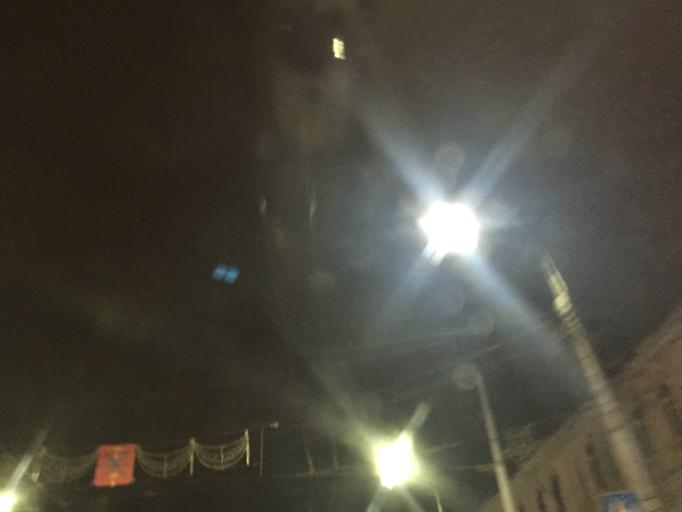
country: RU
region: Tula
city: Tula
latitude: 54.1963
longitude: 37.6121
